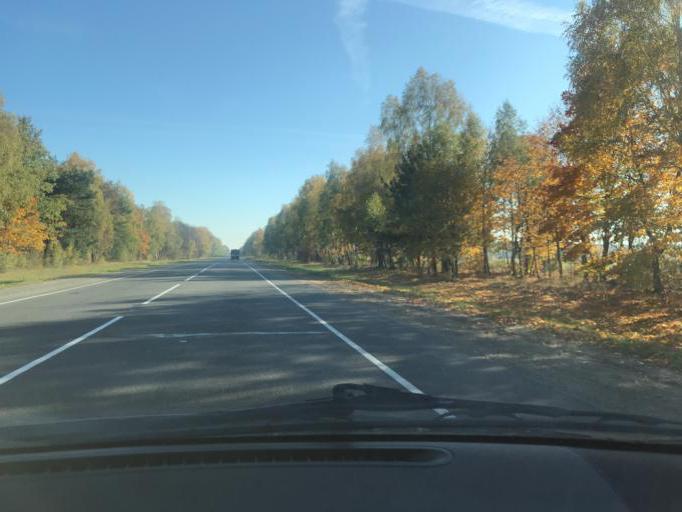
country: BY
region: Brest
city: Ivanava
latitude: 52.1546
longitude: 25.5744
